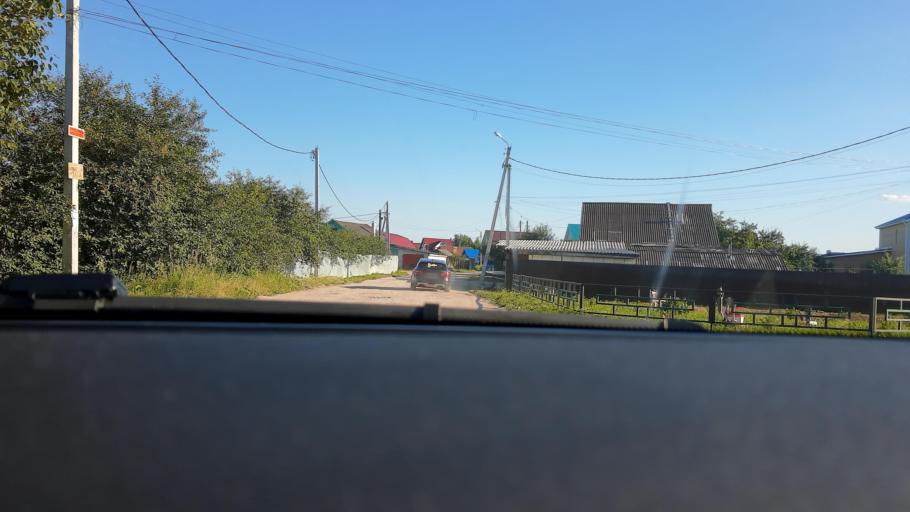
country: RU
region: Nizjnij Novgorod
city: Neklyudovo
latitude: 56.4077
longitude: 44.0339
